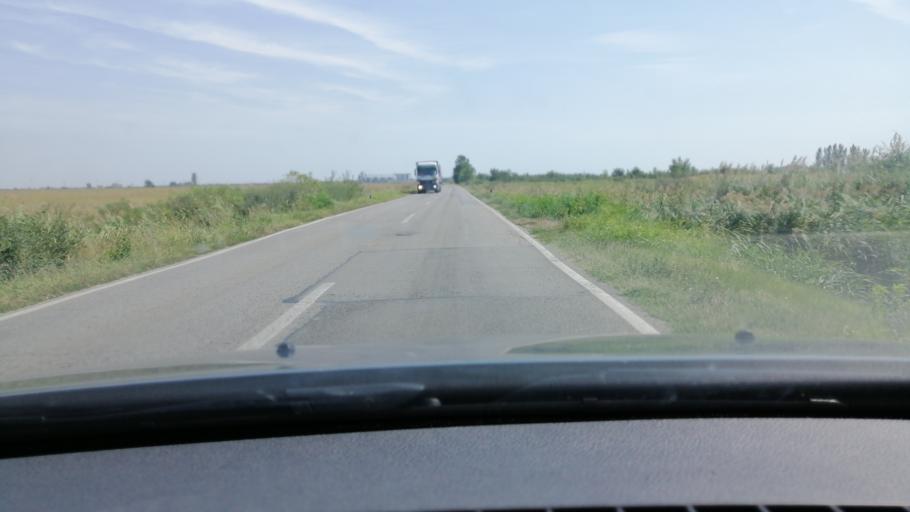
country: RS
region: Autonomna Pokrajina Vojvodina
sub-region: Srednjebanatski Okrug
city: Secanj
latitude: 45.3755
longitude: 20.7371
